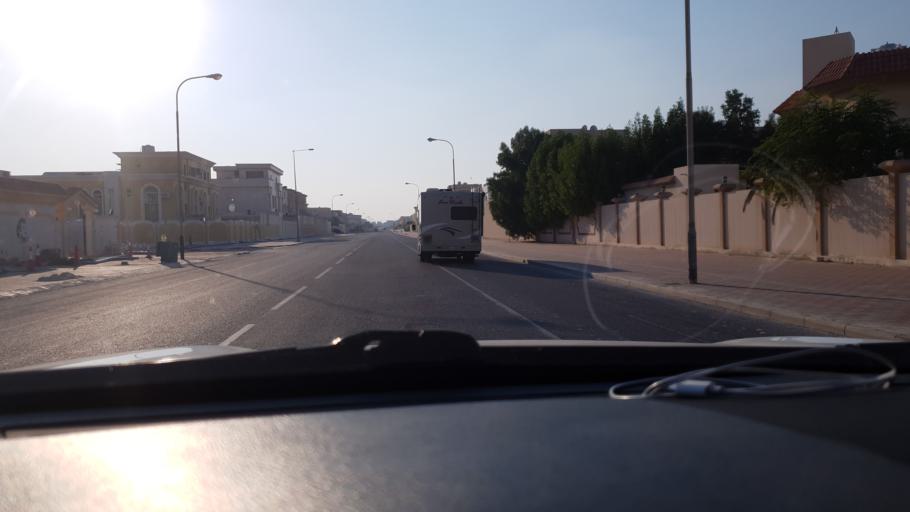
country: QA
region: Baladiyat ad Dawhah
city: Doha
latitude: 25.2332
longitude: 51.5656
